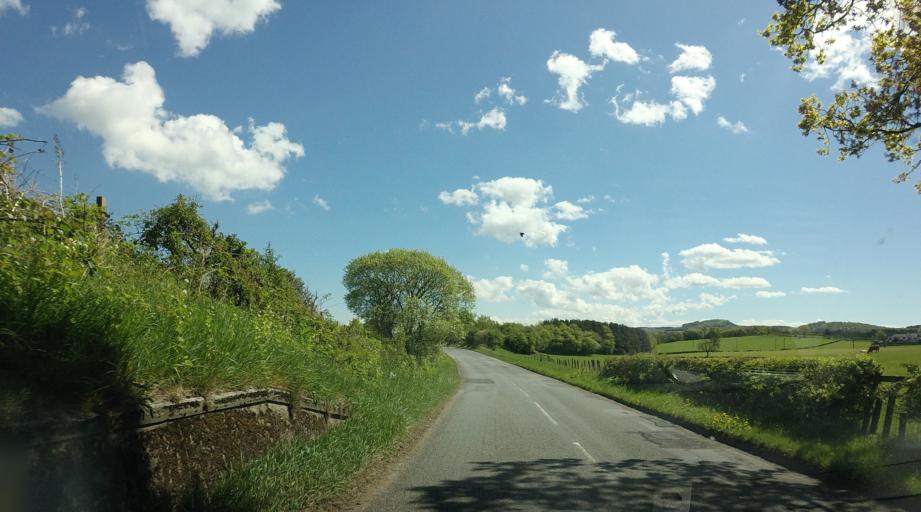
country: GB
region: Scotland
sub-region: Falkirk
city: Polmont
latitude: 55.9725
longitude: -3.6761
